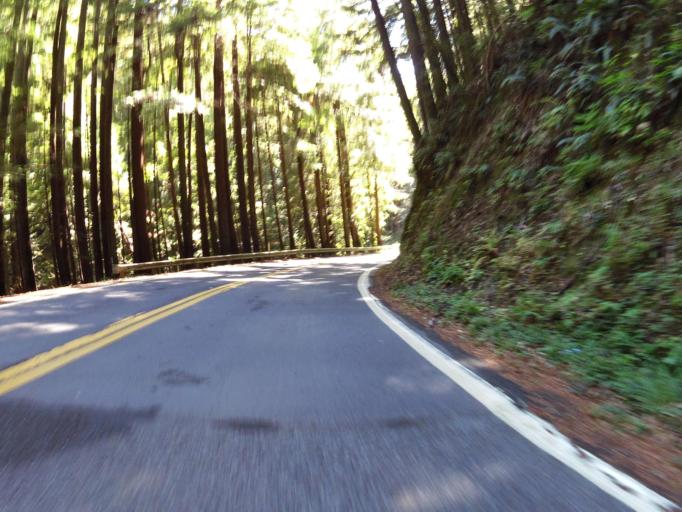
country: US
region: California
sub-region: Humboldt County
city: Redway
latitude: 39.7947
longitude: -123.8169
